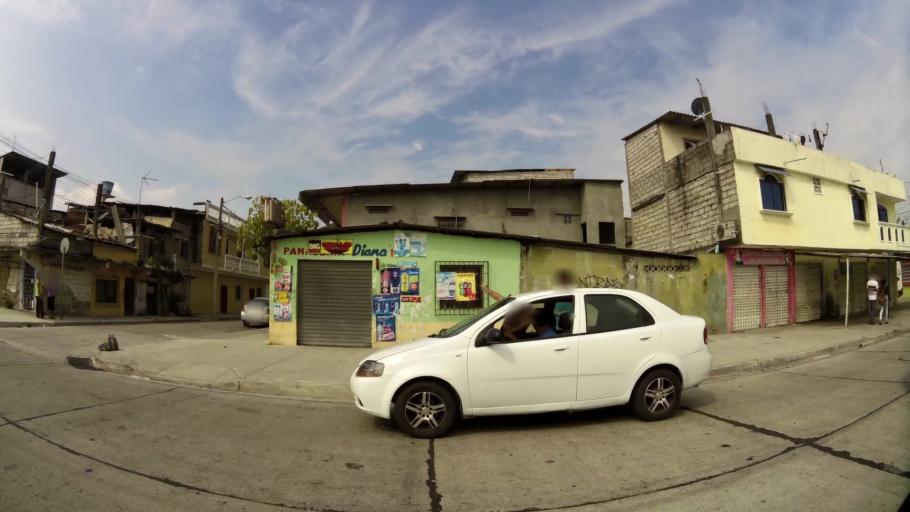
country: EC
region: Guayas
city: Guayaquil
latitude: -2.2531
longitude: -79.8988
